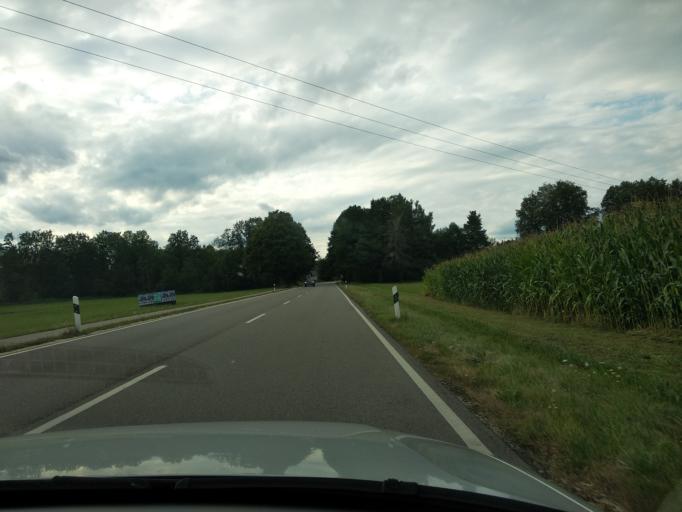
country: DE
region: Bavaria
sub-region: Swabia
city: Benningen
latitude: 47.9753
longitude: 10.2073
